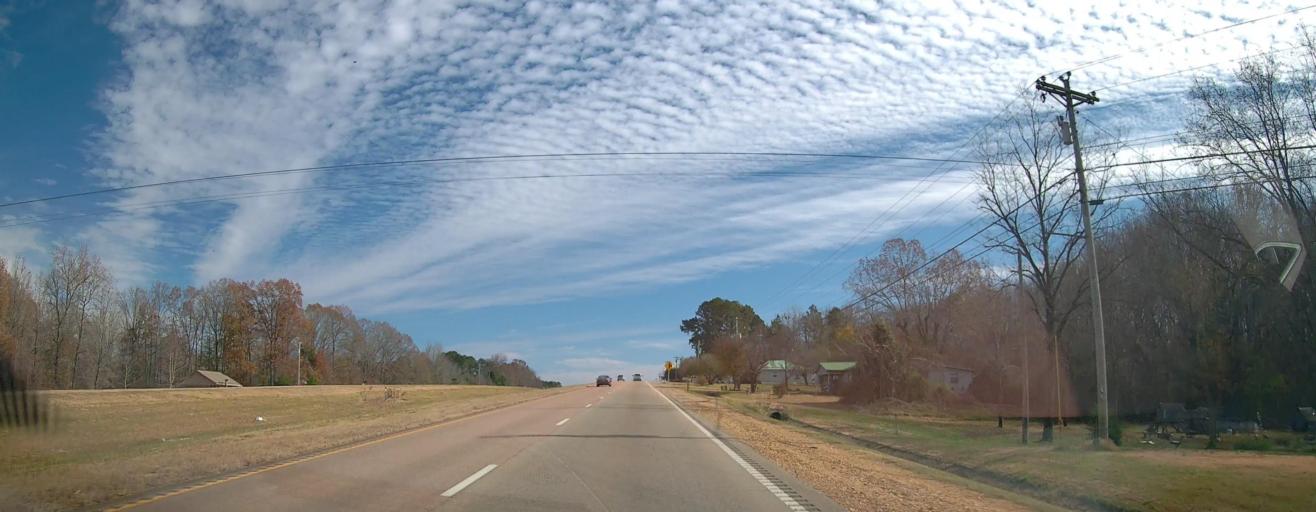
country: US
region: Mississippi
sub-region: Tippah County
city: Ripley
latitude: 34.9545
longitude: -88.8450
